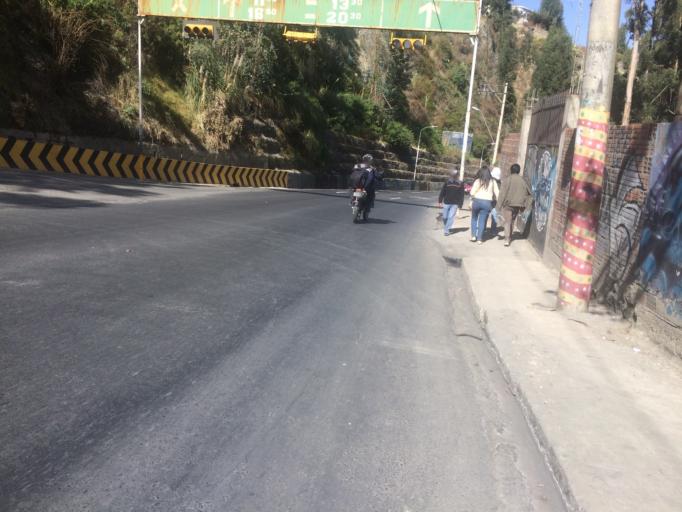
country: BO
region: La Paz
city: La Paz
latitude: -16.5133
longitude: -68.1183
